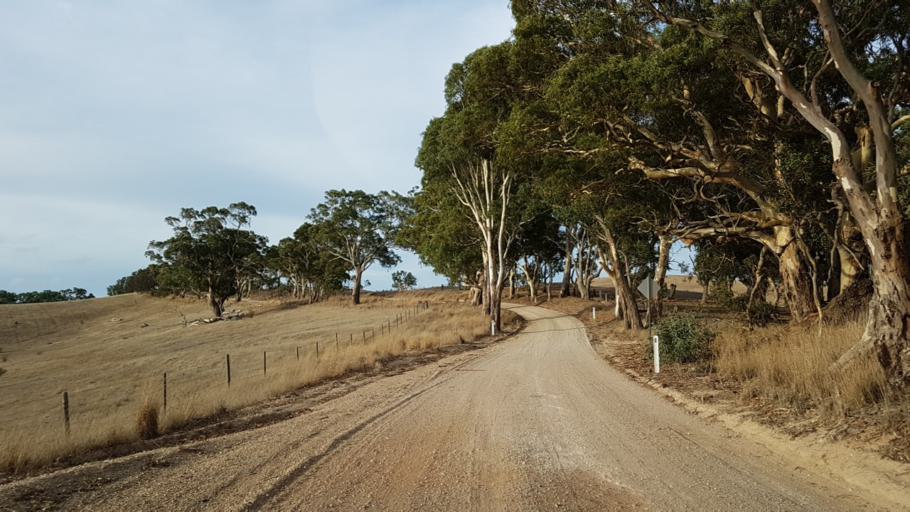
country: AU
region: South Australia
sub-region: Mount Barker
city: Nairne
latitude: -35.0190
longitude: 138.9095
